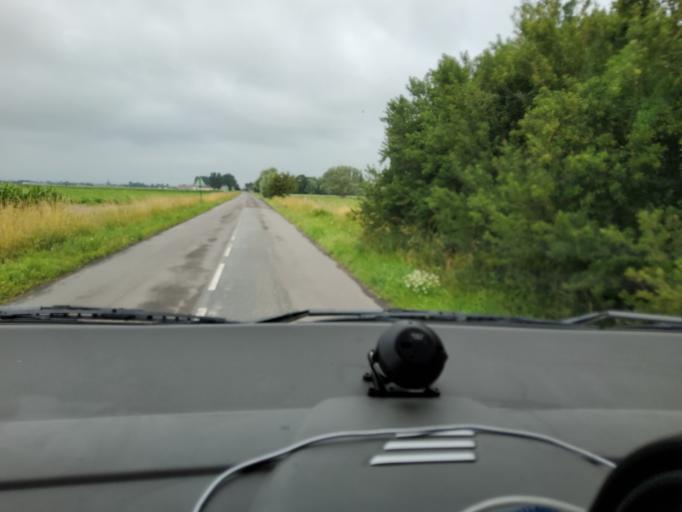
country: FR
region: Nord-Pas-de-Calais
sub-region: Departement du Pas-de-Calais
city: Sainte-Marie-Kerque
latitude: 50.9116
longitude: 2.1645
